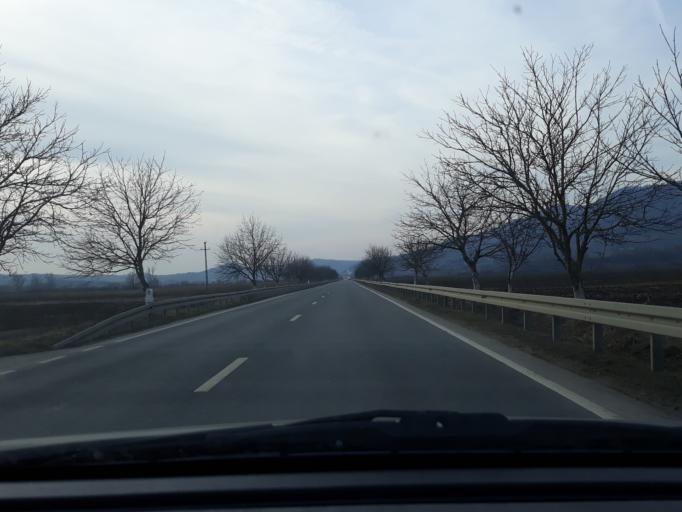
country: RO
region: Salaj
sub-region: Comuna Periceiu
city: Periceiu
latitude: 47.2283
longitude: 22.8454
